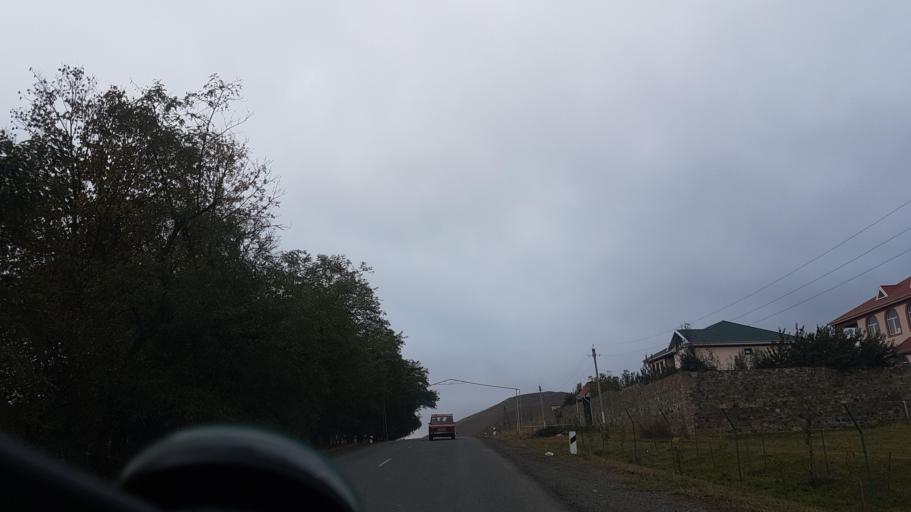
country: AZ
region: Gadabay Rayon
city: Ariqdam
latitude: 40.6217
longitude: 45.8138
